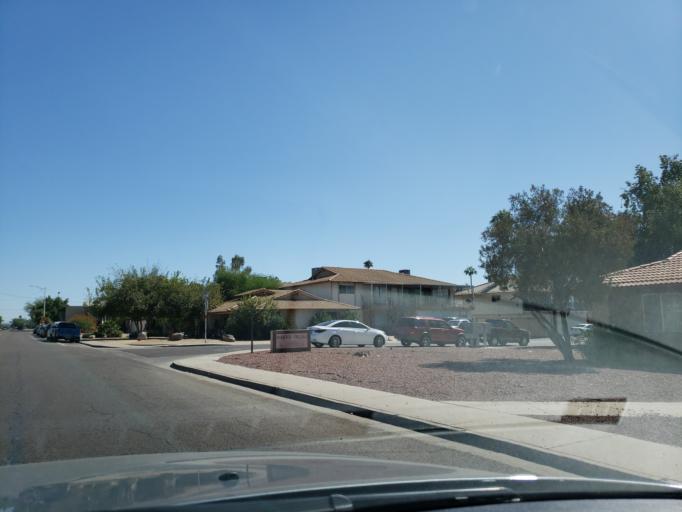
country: US
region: Arizona
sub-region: Maricopa County
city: Glendale
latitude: 33.5022
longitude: -112.1745
